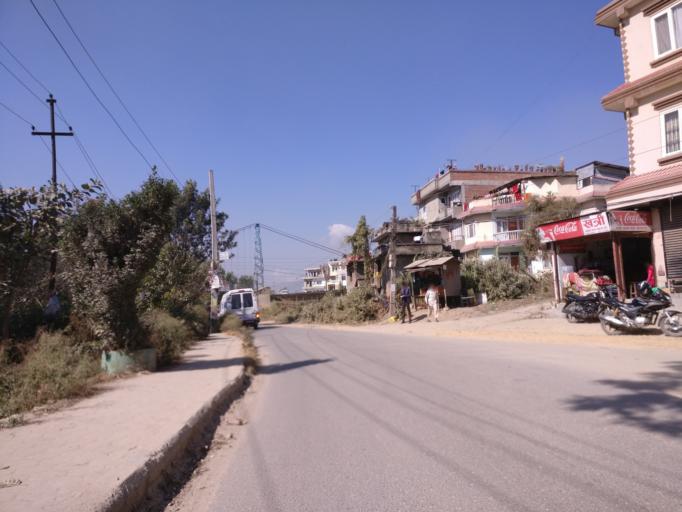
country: NP
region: Central Region
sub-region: Bagmati Zone
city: Patan
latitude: 27.6755
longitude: 85.3392
